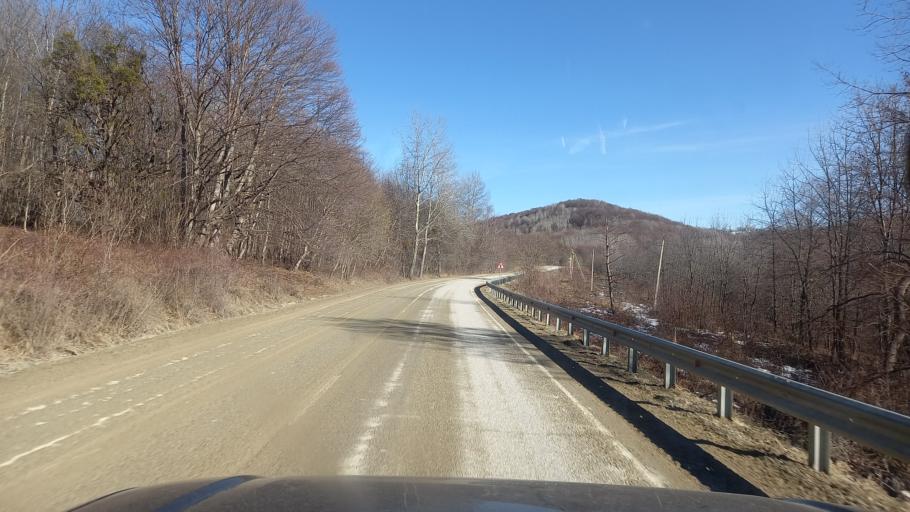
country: RU
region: Adygeya
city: Kamennomostskiy
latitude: 44.2852
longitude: 40.2957
